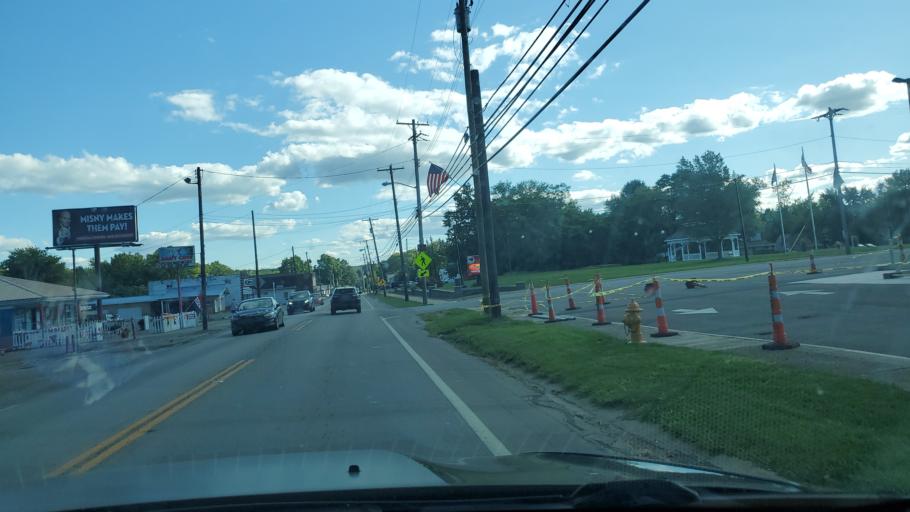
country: US
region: Ohio
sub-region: Trumbull County
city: Mineral Ridge
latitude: 41.1416
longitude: -80.7689
